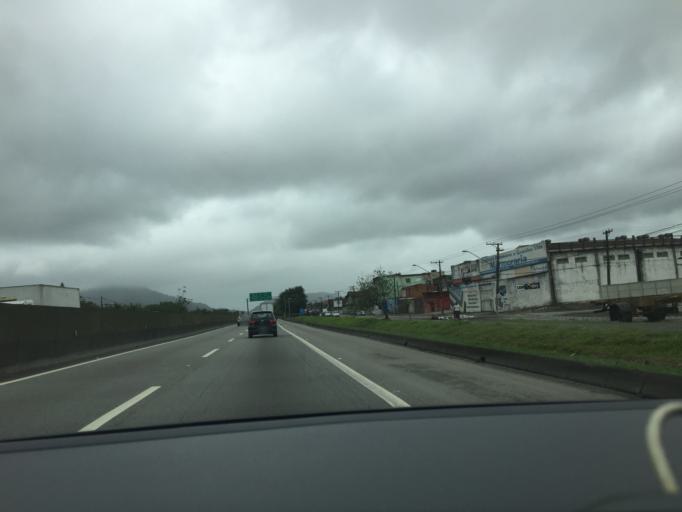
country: BR
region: Sao Paulo
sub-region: Guaruja
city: Guaruja
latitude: -23.9499
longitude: -46.2774
